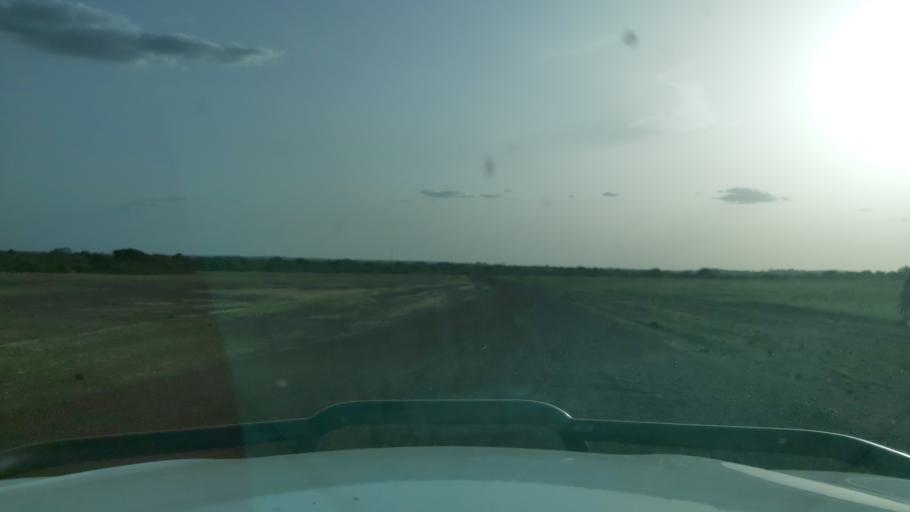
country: ML
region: Koulikoro
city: Kolokani
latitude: 13.2086
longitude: -7.9088
